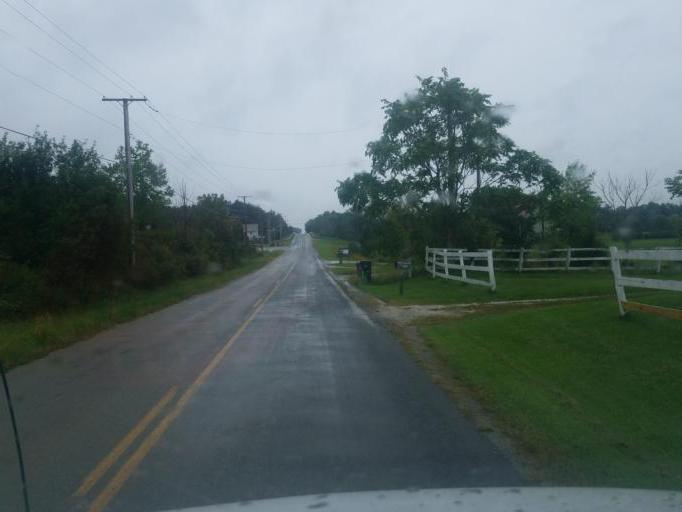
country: US
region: Ohio
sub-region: Medina County
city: Seville
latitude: 41.0351
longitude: -81.8324
